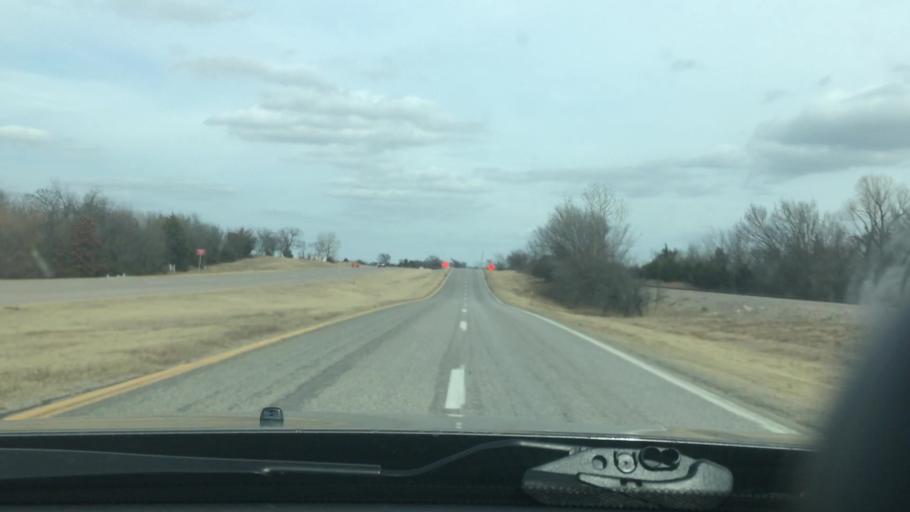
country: US
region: Oklahoma
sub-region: Pontotoc County
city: Ada
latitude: 34.6999
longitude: -96.7349
